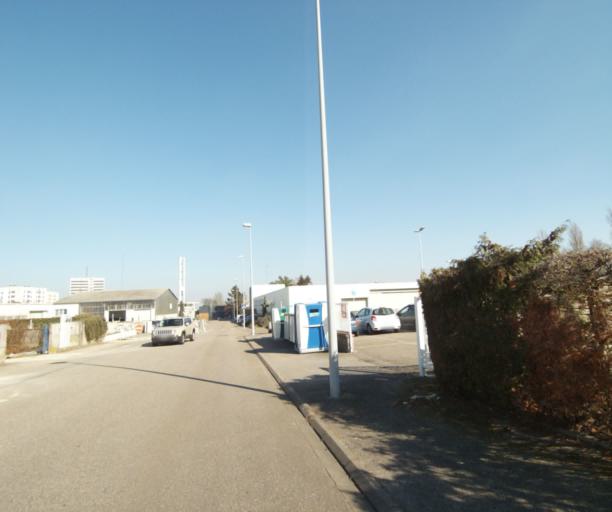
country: FR
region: Lorraine
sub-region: Departement de Meurthe-et-Moselle
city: Vandoeuvre-les-Nancy
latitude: 48.6583
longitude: 6.1827
